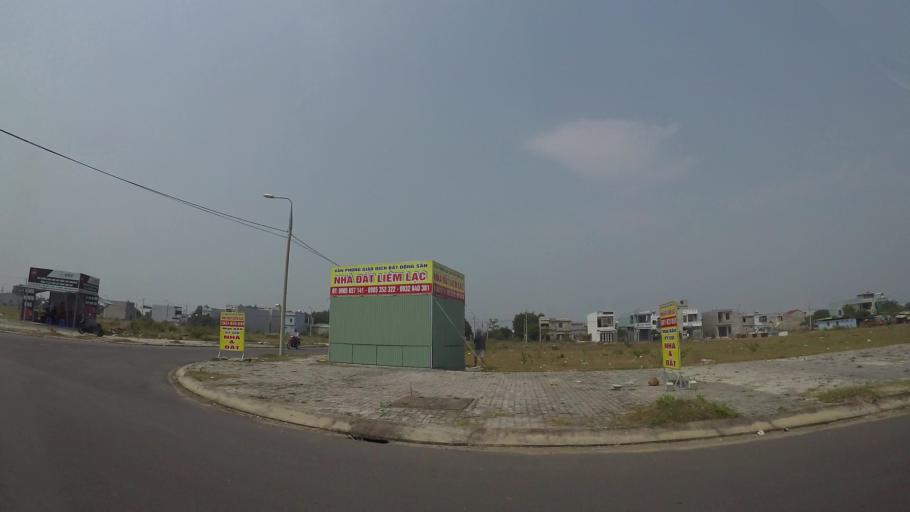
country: VN
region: Da Nang
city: Cam Le
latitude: 15.9816
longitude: 108.2171
